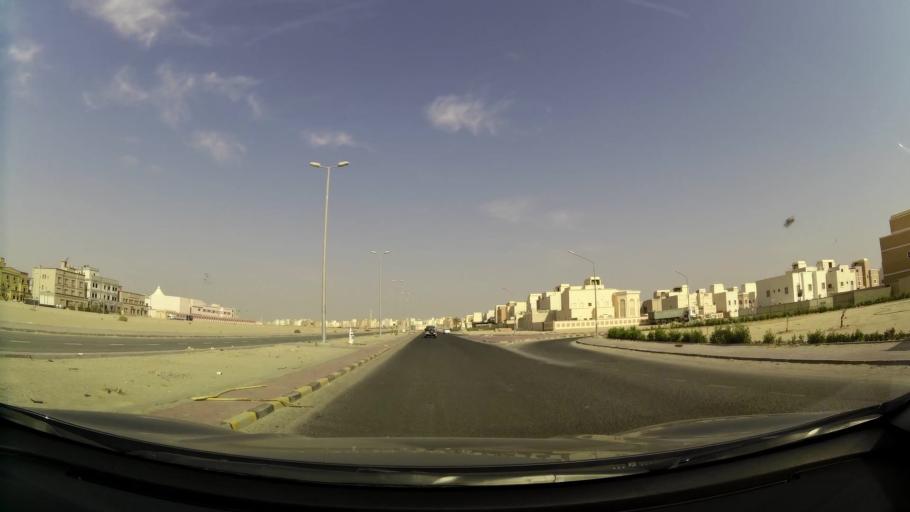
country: KW
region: Al Ahmadi
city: Al Wafrah
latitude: 28.7917
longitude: 48.0668
